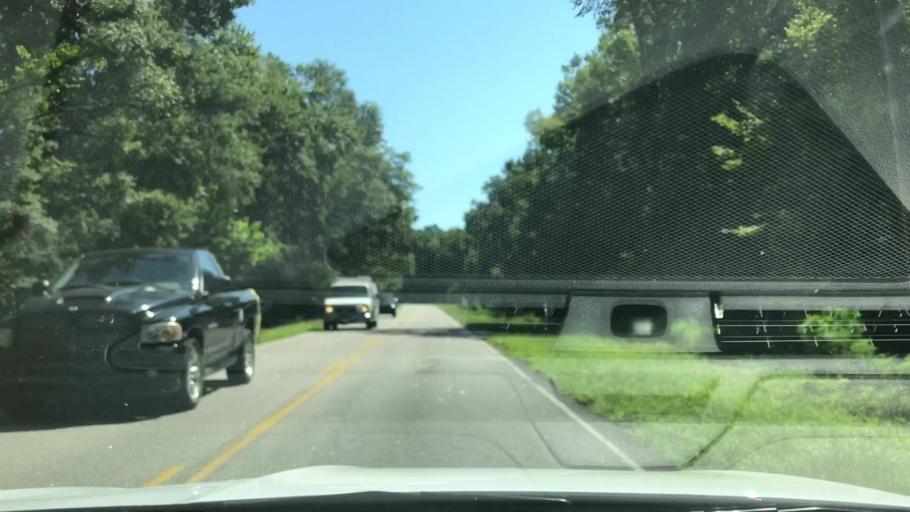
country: US
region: South Carolina
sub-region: Horry County
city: Conway
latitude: 33.8392
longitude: -79.0359
